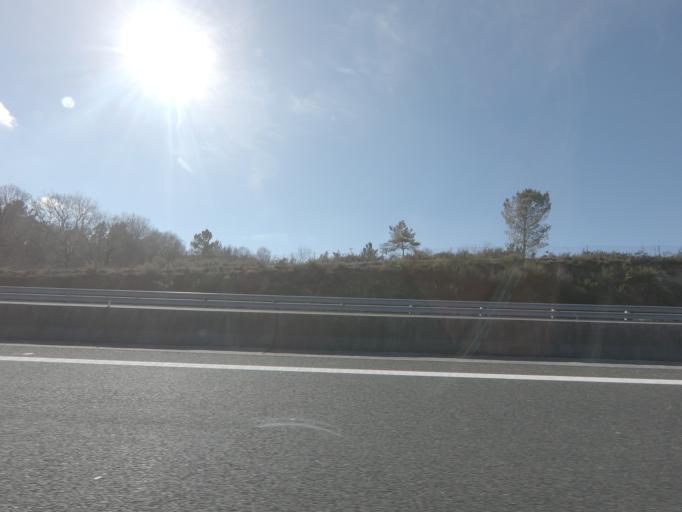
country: ES
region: Galicia
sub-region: Provincia de Pontevedra
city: Dozon
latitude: 42.5407
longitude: -8.0190
